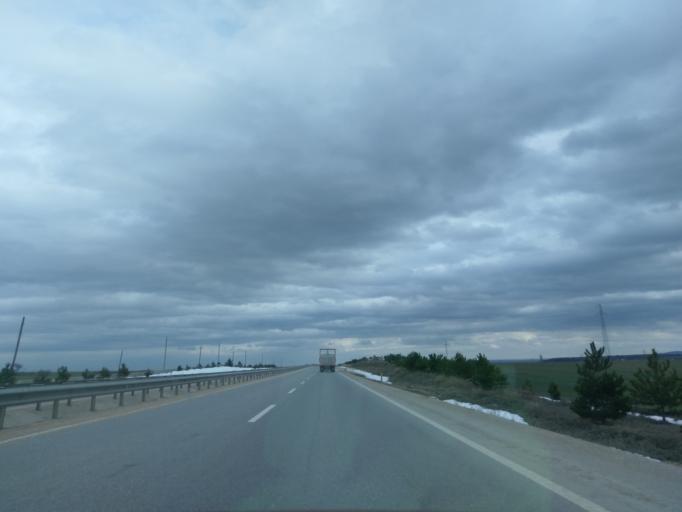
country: TR
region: Eskisehir
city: Inonu
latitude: 39.7241
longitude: 30.2751
